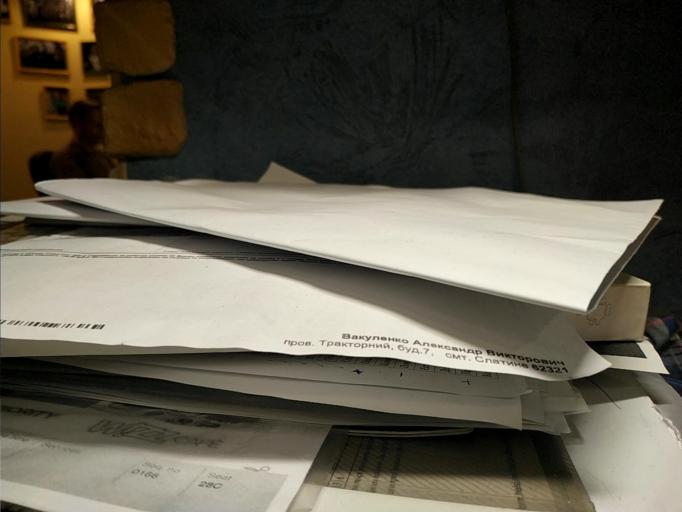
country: RU
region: Tverskaya
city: Zubtsov
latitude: 56.1358
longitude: 34.4835
